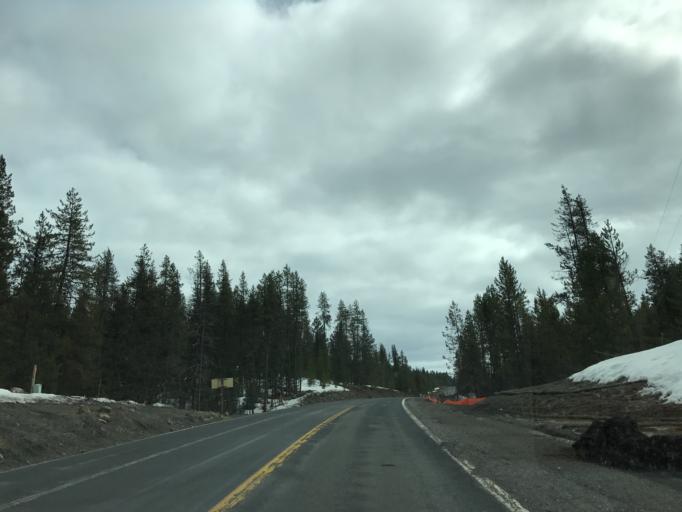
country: US
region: Idaho
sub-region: Valley County
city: McCall
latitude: 44.9575
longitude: -116.1706
